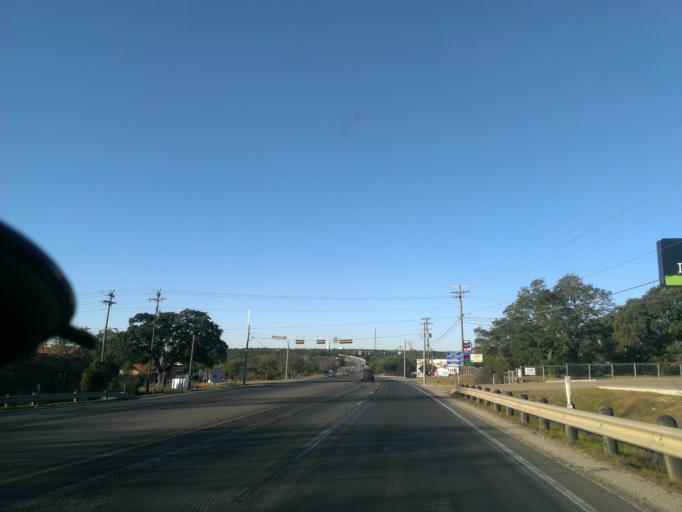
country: US
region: Texas
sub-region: Travis County
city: Bee Cave
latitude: 30.2226
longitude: -97.9551
